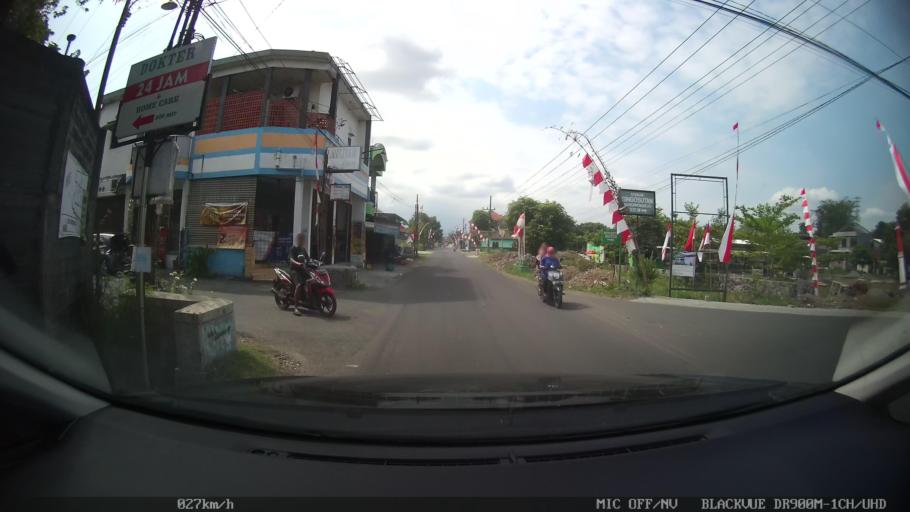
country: ID
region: Daerah Istimewa Yogyakarta
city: Depok
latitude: -7.7674
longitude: 110.4390
